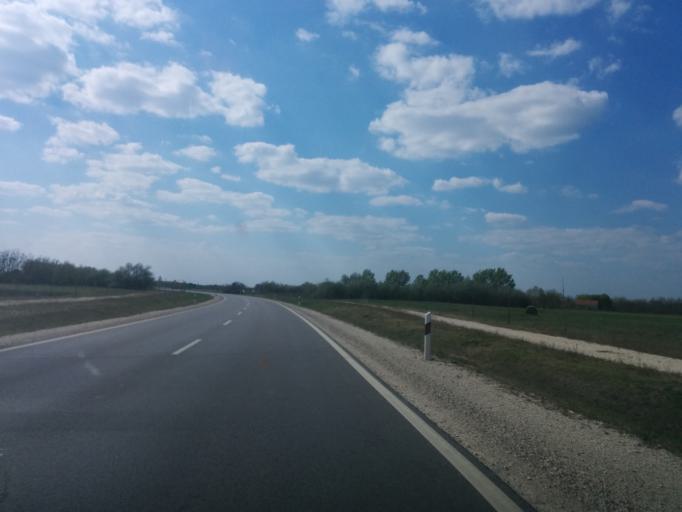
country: HU
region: Csongrad
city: Morahalom
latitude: 46.2369
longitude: 19.8819
